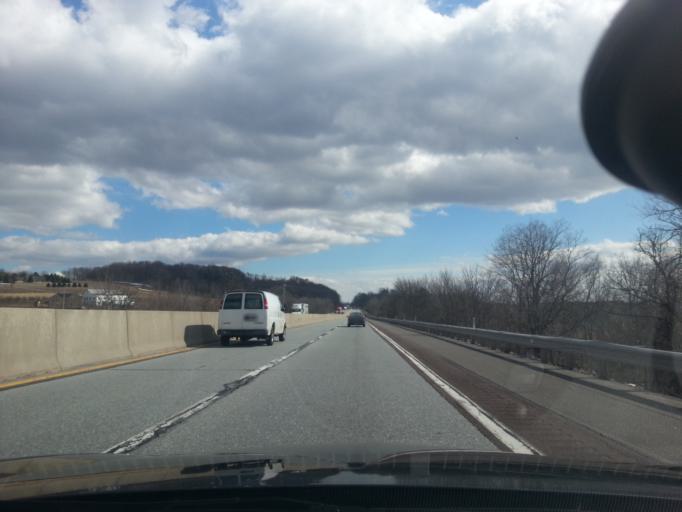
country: US
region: Pennsylvania
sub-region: Bucks County
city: Spinnerstown
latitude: 40.4840
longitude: -75.4634
